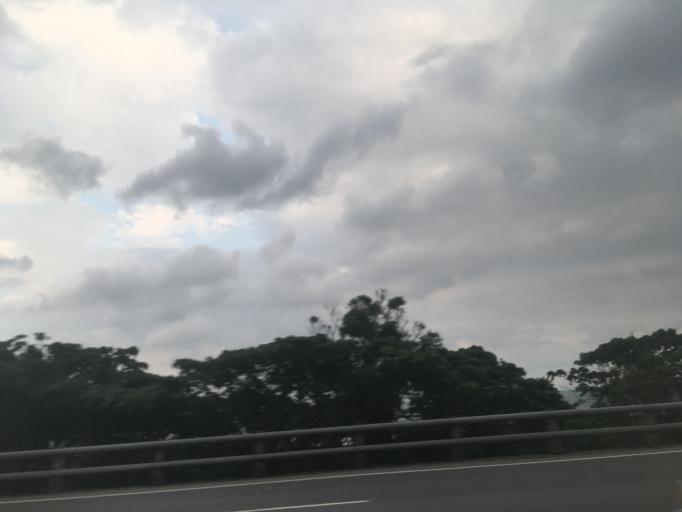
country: TW
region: Taiwan
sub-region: Yilan
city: Yilan
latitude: 24.9309
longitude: 121.8848
